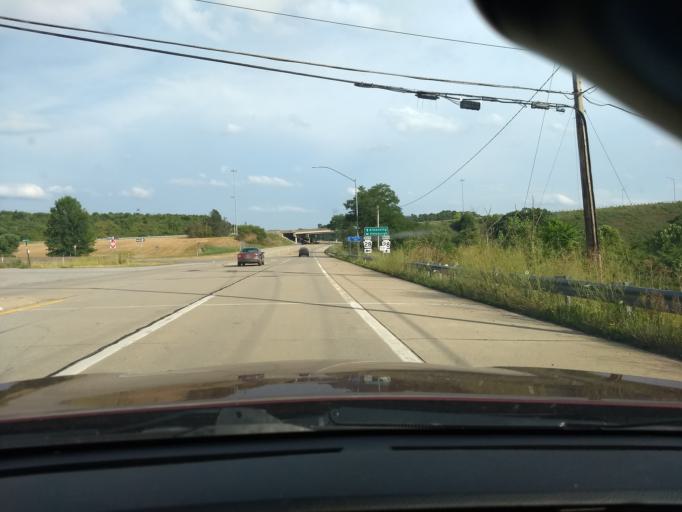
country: US
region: Pennsylvania
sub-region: Allegheny County
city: Tarentum
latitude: 40.6154
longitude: -79.7595
